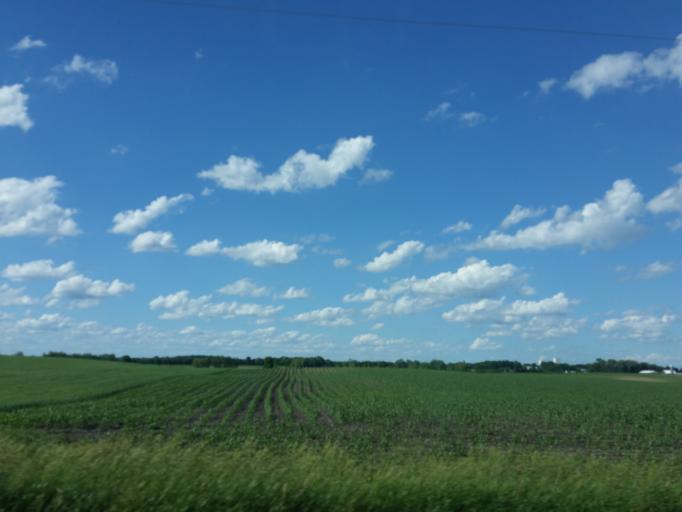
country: US
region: Minnesota
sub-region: Wright County
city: Cokato
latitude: 45.0662
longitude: -94.2463
